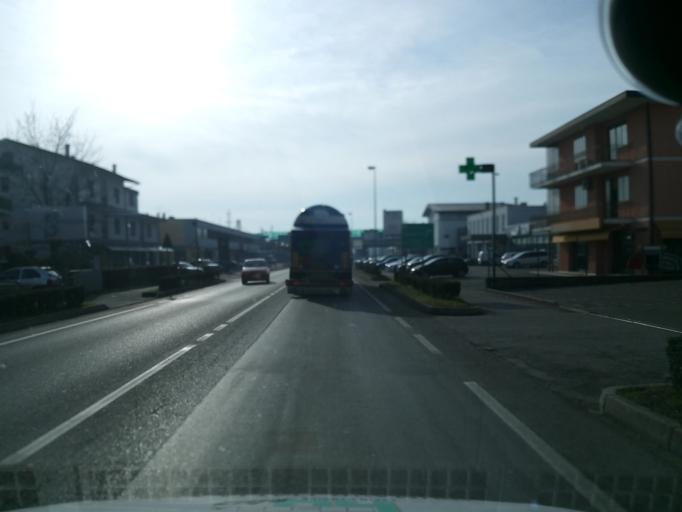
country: IT
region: Veneto
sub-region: Provincia di Vicenza
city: Dueville
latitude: 45.6410
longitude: 11.5748
